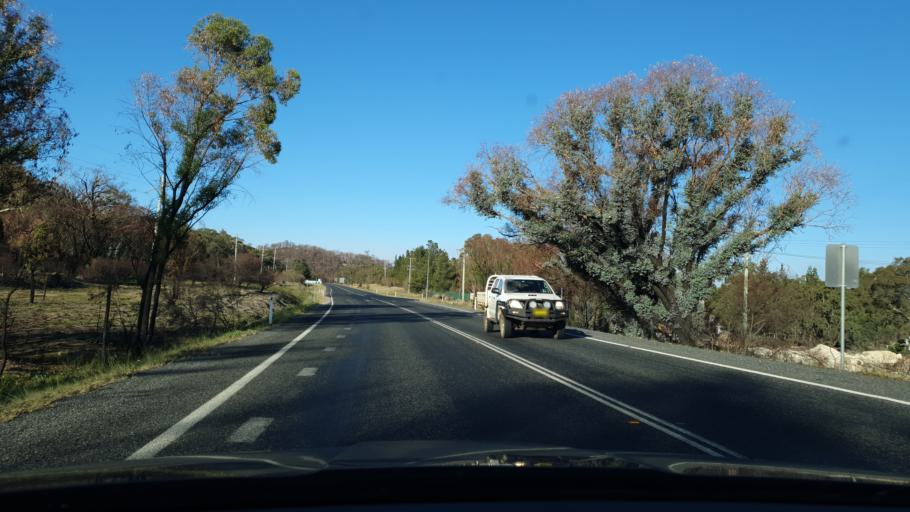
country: AU
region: Queensland
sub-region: Southern Downs
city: Stanthorpe
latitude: -28.6499
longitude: 151.9223
